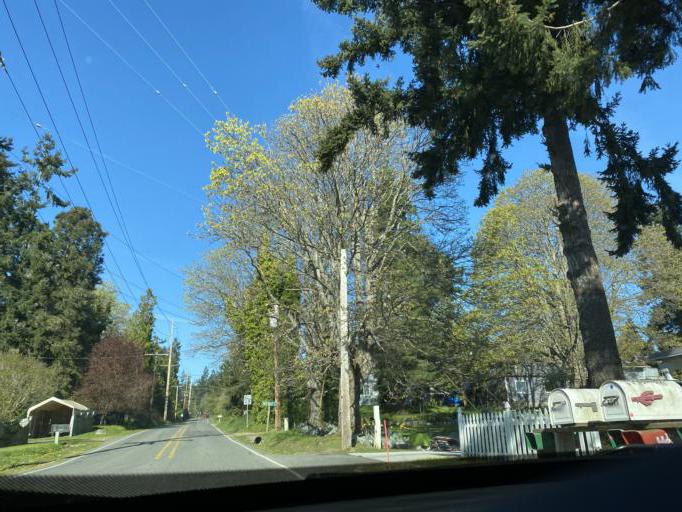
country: US
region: Washington
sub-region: Island County
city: Freeland
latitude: 48.0155
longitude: -122.5410
